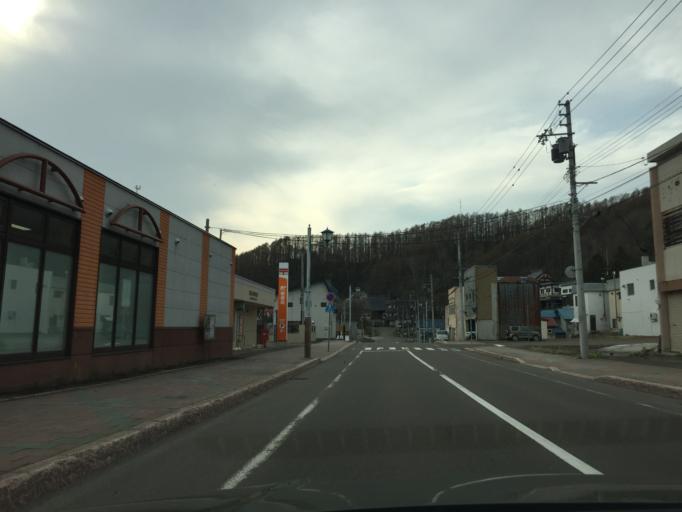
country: JP
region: Hokkaido
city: Utashinai
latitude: 43.5219
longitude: 142.0413
